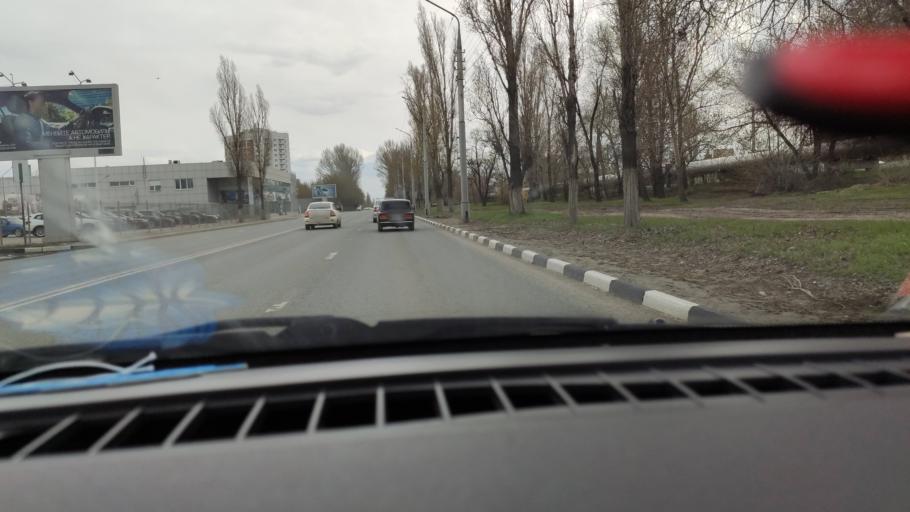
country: RU
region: Saratov
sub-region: Saratovskiy Rayon
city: Saratov
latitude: 51.5725
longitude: 45.9923
